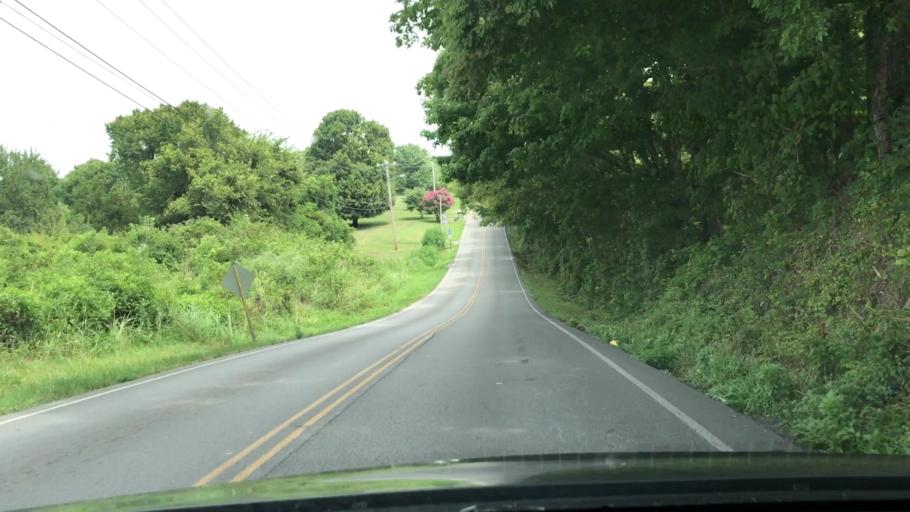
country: US
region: Tennessee
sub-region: Rutherford County
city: La Vergne
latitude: 35.9659
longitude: -86.6011
